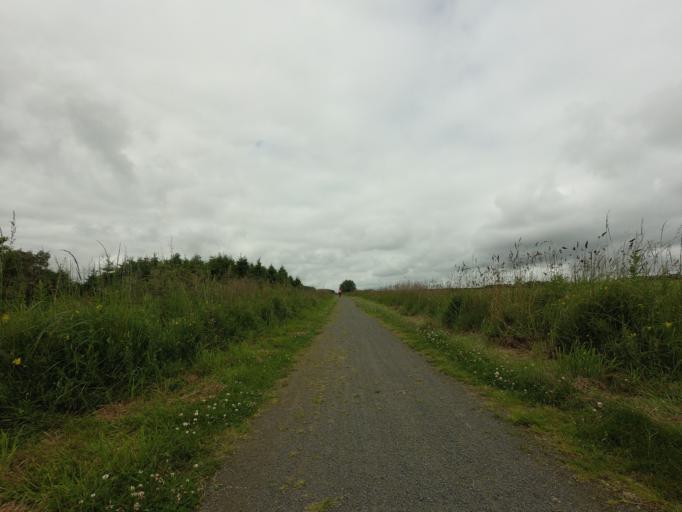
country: GB
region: Scotland
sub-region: Aberdeenshire
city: Mintlaw
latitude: 57.4930
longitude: -2.1361
